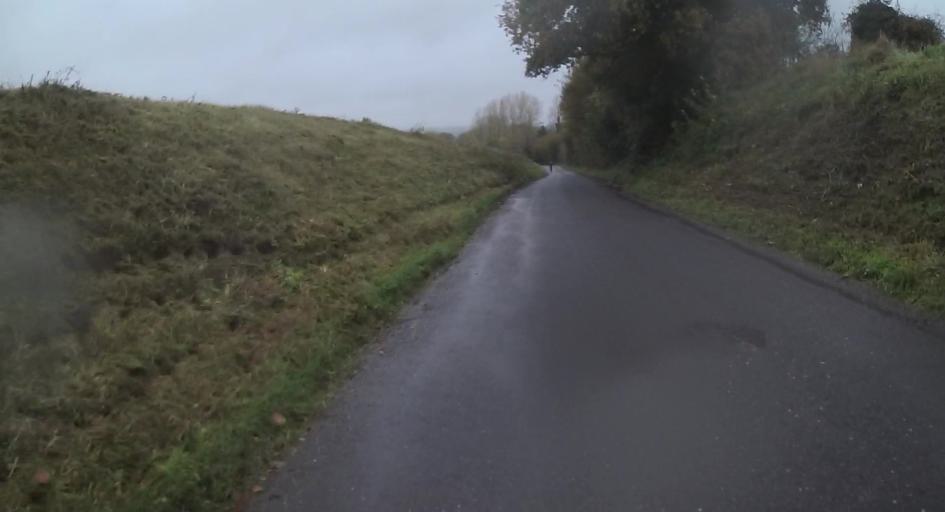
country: GB
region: England
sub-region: Hampshire
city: Kingsley
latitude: 51.1704
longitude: -0.8994
